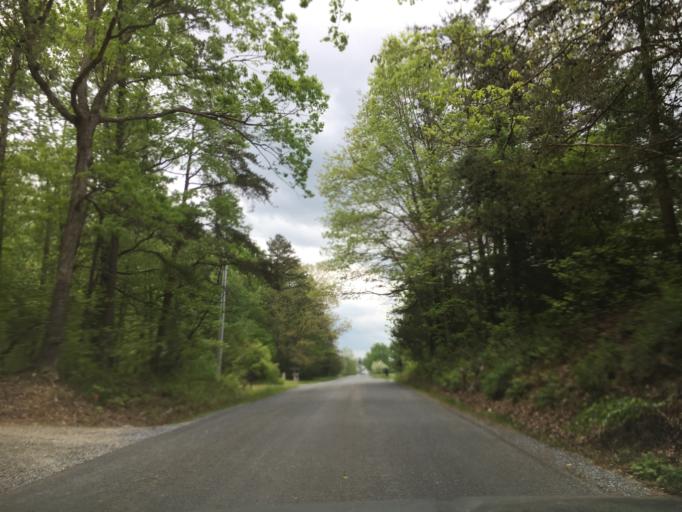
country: US
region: Virginia
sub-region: Campbell County
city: Rustburg
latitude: 37.2061
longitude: -79.0444
